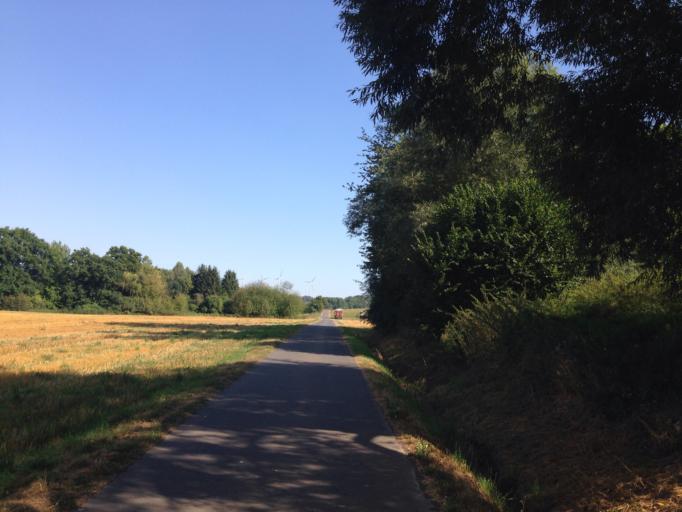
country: DE
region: Hesse
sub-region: Regierungsbezirk Giessen
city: Rabenau
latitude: 50.6700
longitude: 8.8641
